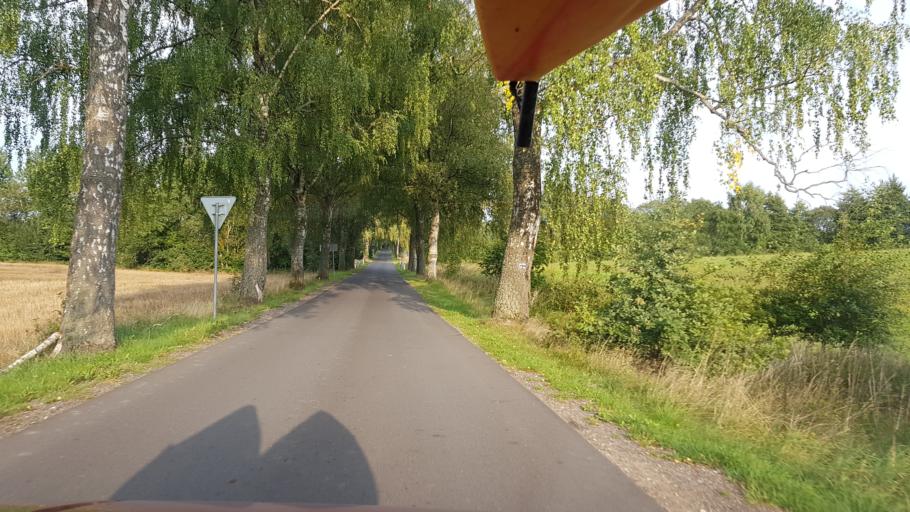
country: PL
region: West Pomeranian Voivodeship
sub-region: Powiat szczecinecki
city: Bialy Bor
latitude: 54.0208
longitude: 16.8363
